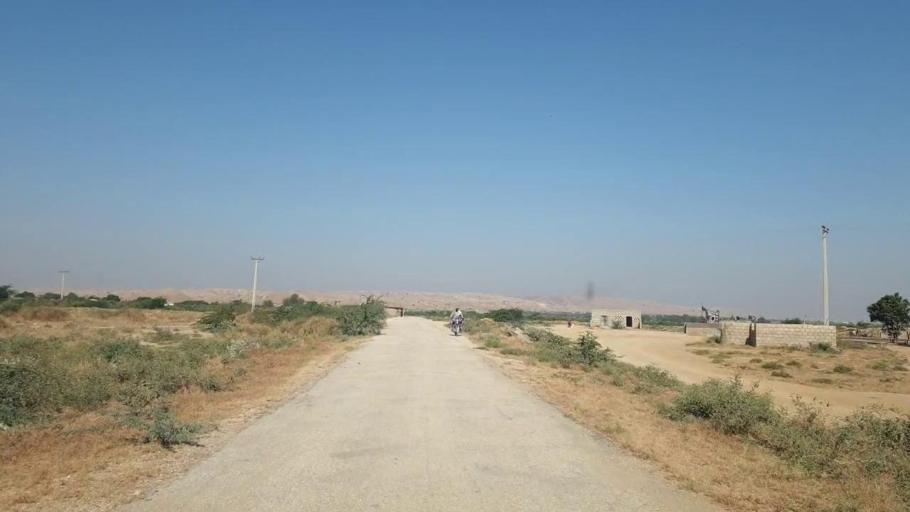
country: PK
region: Sindh
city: Gharo
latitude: 25.1722
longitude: 67.7329
